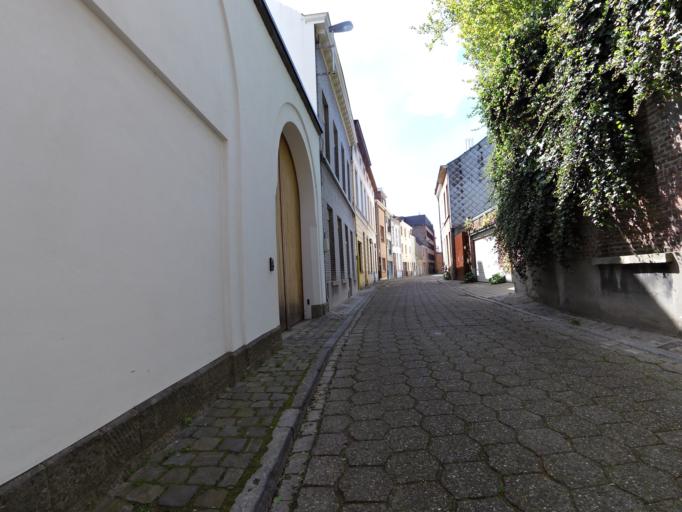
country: BE
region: Flanders
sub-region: Provincie Oost-Vlaanderen
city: Gent
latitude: 51.0505
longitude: 3.7168
